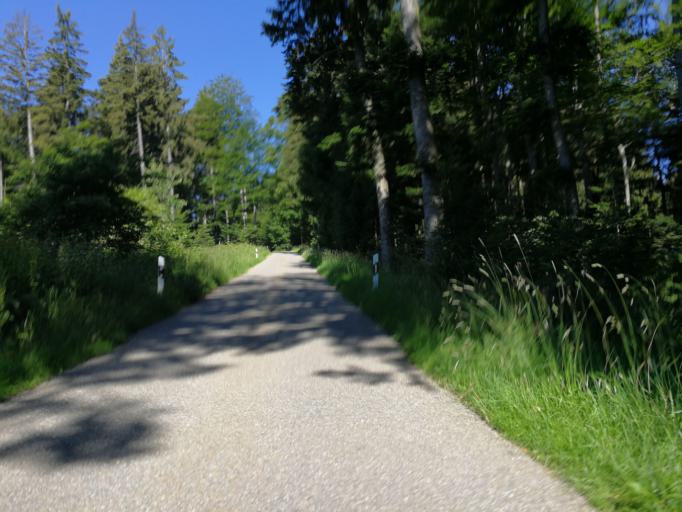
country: CH
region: Zurich
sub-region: Bezirk Hinwil
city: Wald
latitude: 47.2935
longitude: 8.8911
